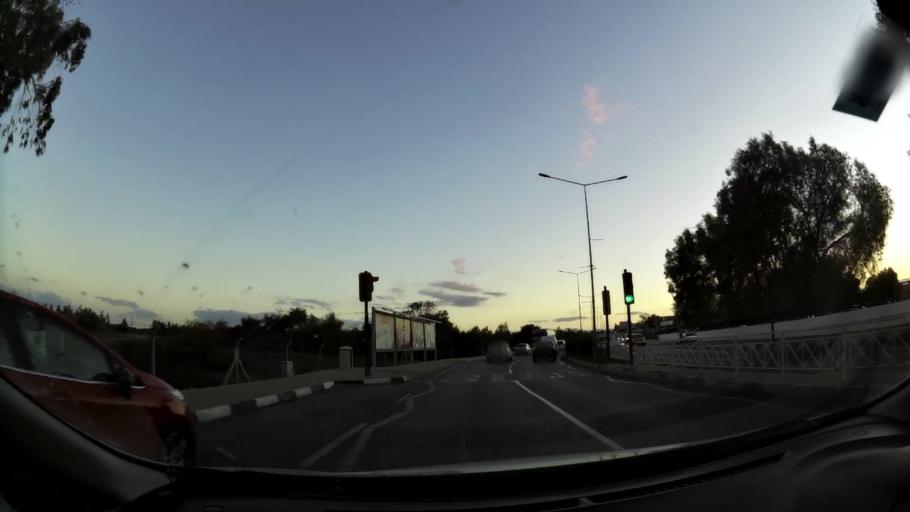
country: CY
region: Lefkosia
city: Nicosia
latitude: 35.1958
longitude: 33.3313
